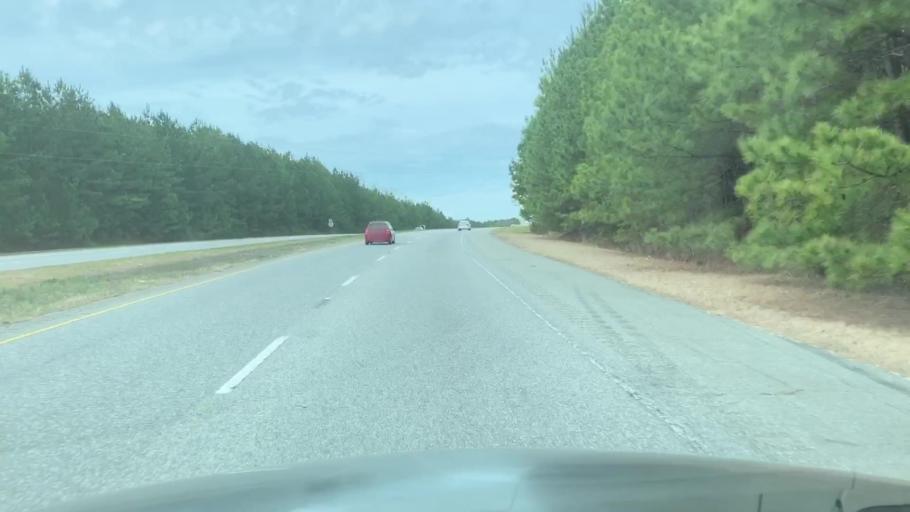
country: US
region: South Carolina
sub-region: Greenville County
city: Golden Grove
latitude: 34.7330
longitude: -82.4257
